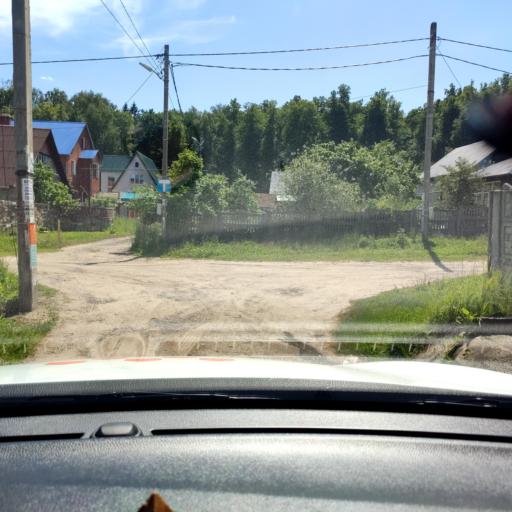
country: RU
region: Tatarstan
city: Osinovo
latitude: 55.8506
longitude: 48.8799
